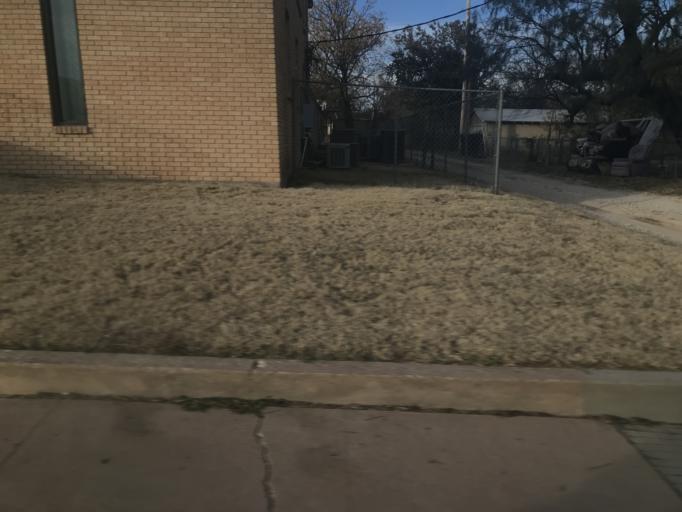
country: US
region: Texas
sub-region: Taylor County
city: Abilene
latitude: 32.4322
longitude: -99.7439
